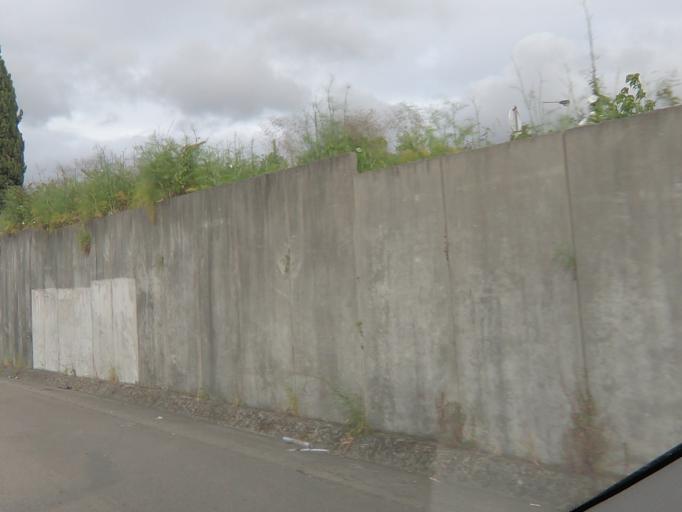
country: PT
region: Porto
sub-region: Gondomar
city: Rio Tinto
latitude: 41.1651
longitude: -8.5782
